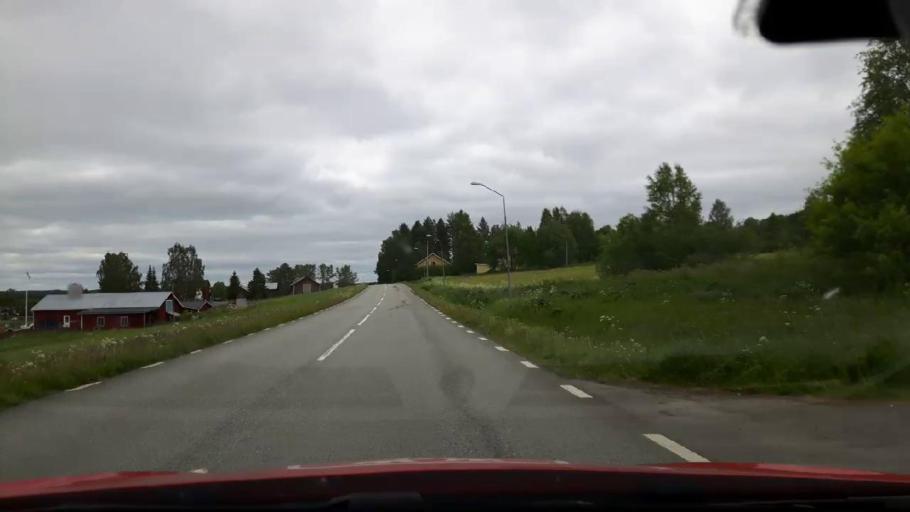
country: SE
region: Jaemtland
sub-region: Stroemsunds Kommun
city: Stroemsund
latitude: 63.5620
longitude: 15.3973
